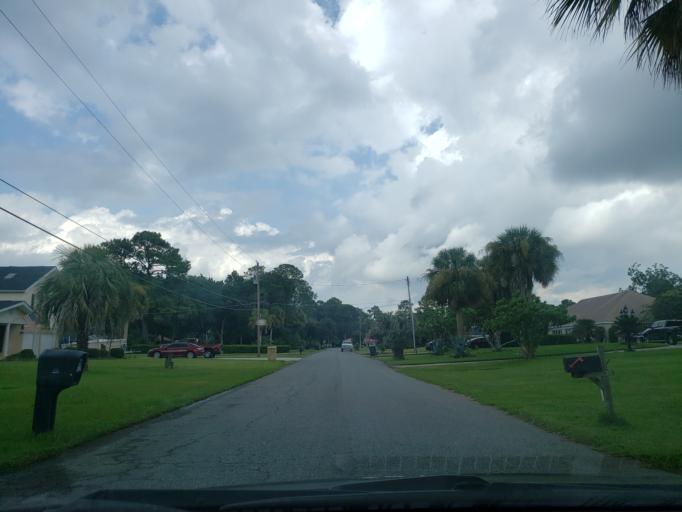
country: US
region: Georgia
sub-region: Chatham County
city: Montgomery
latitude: 31.9277
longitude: -81.0889
